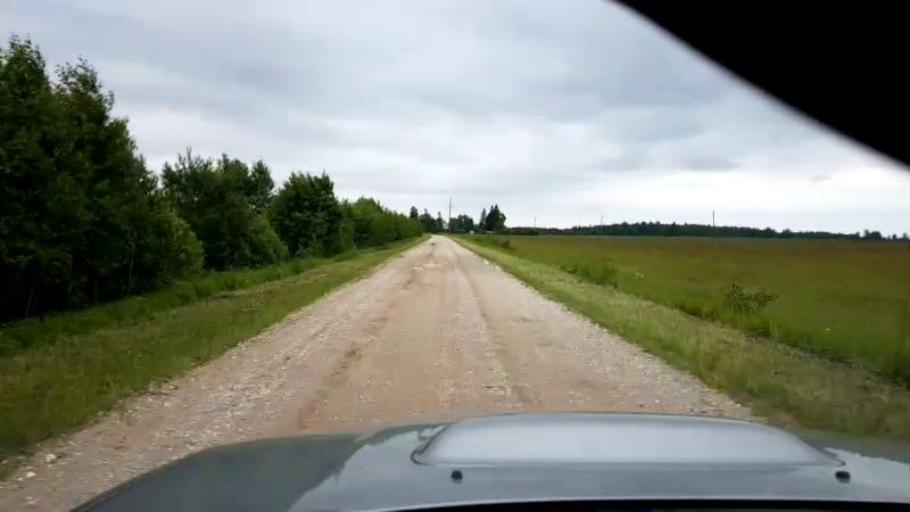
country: EE
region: Paernumaa
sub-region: Halinga vald
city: Parnu-Jaagupi
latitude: 58.5431
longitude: 24.5589
